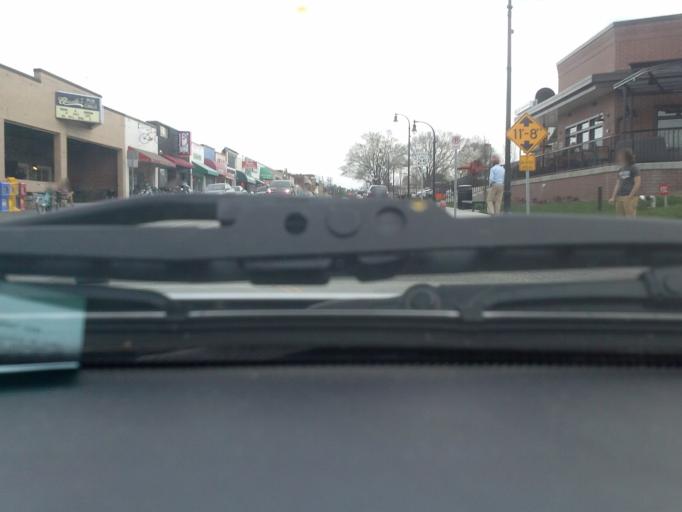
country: US
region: North Carolina
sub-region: Durham County
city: Durham
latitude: 36.0101
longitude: -78.9221
